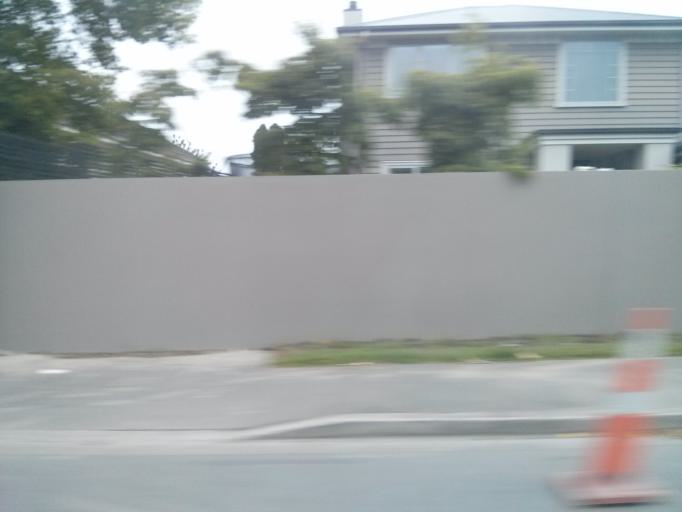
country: NZ
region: Canterbury
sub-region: Christchurch City
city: Christchurch
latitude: -43.5204
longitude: 172.6012
